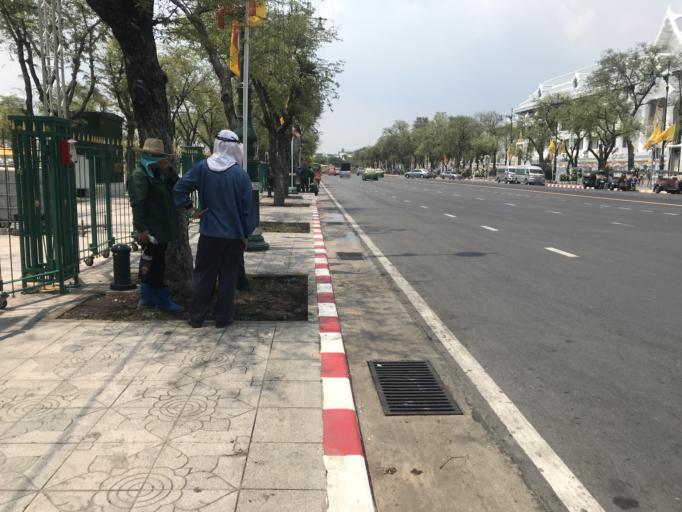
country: TH
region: Bangkok
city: Bangkok
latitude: 13.7534
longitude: 100.4936
